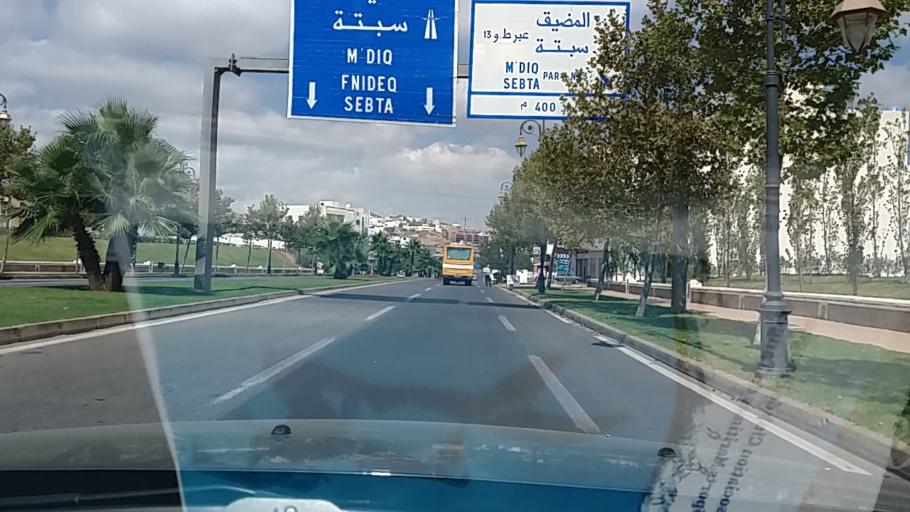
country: MA
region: Tanger-Tetouan
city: Tetouan
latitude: 35.5930
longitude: -5.3364
